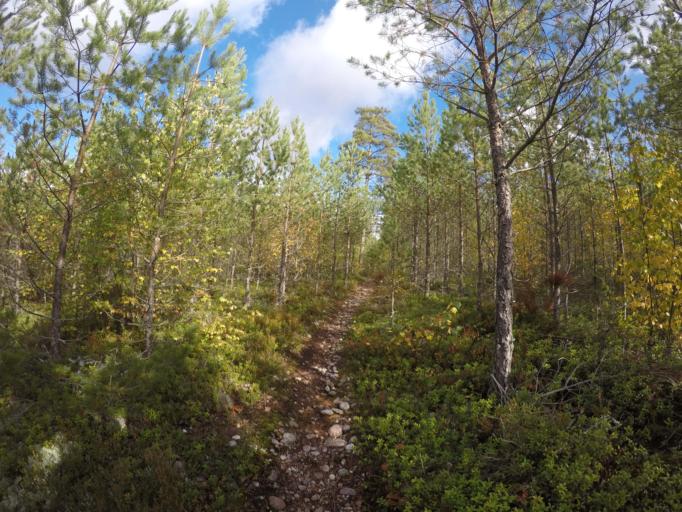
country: SE
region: Vaestmanland
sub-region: Kungsors Kommun
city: Kungsoer
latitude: 59.3140
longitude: 16.1124
